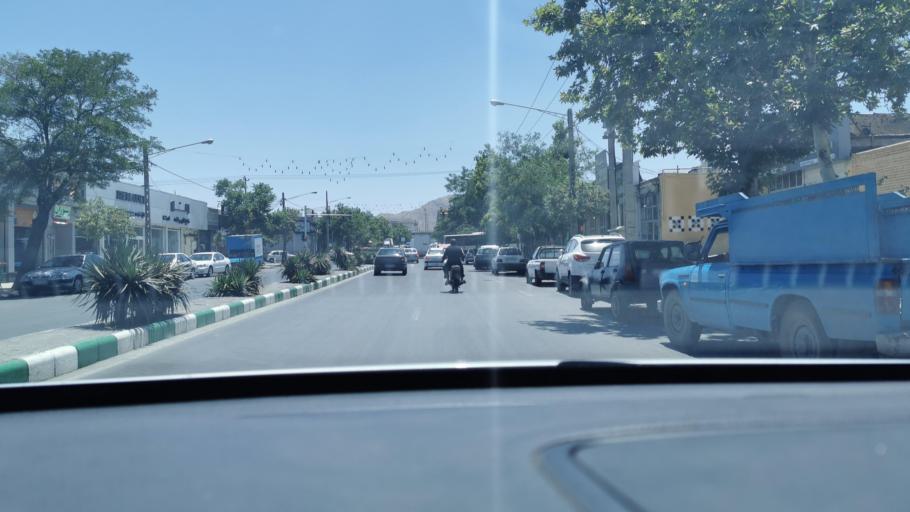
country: IR
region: Razavi Khorasan
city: Mashhad
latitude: 36.2609
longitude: 59.6031
